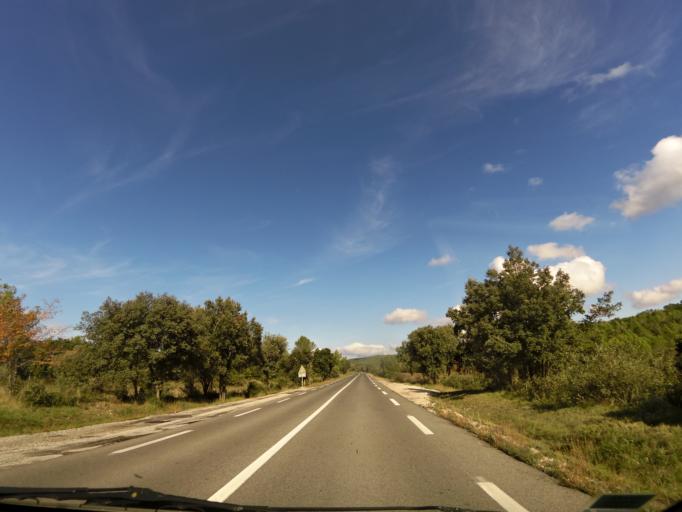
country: FR
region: Languedoc-Roussillon
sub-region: Departement du Gard
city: Villevieille
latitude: 43.8586
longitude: 4.0971
